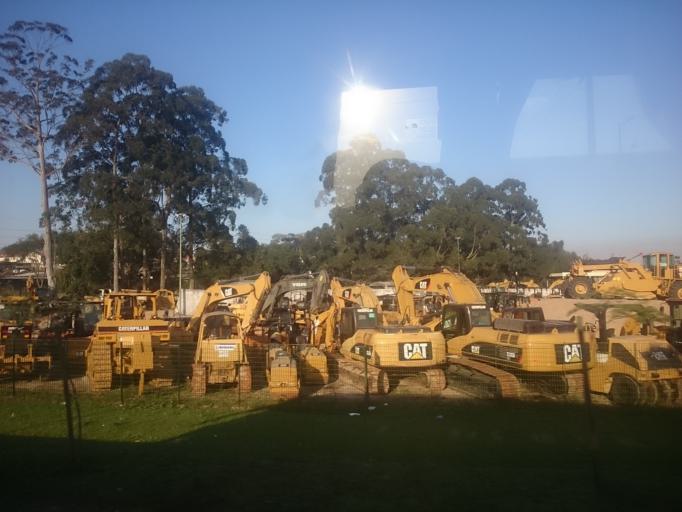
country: BR
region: Parana
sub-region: Curitiba
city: Curitiba
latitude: -25.4653
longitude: -49.2520
